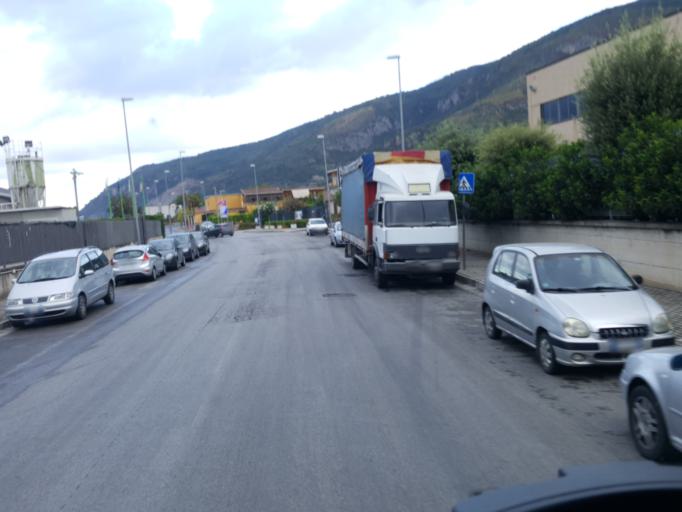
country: IT
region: Campania
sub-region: Provincia di Napoli
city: Striano
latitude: 40.8216
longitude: 14.5996
